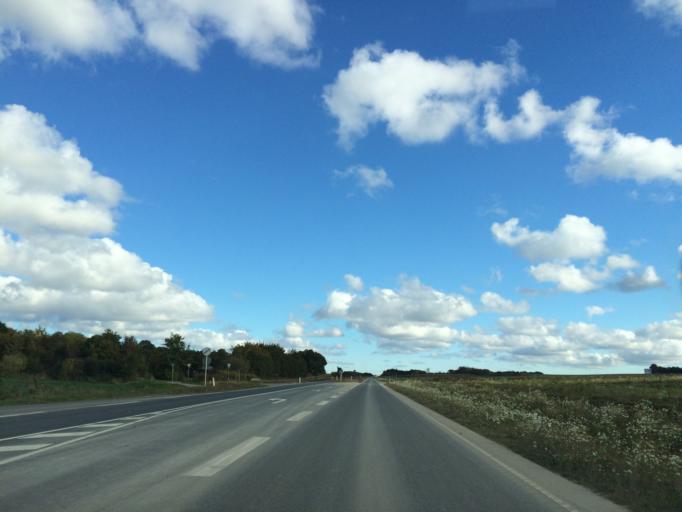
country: DK
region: Central Jutland
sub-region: Skanderborg Kommune
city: Ry
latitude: 56.1490
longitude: 9.7796
